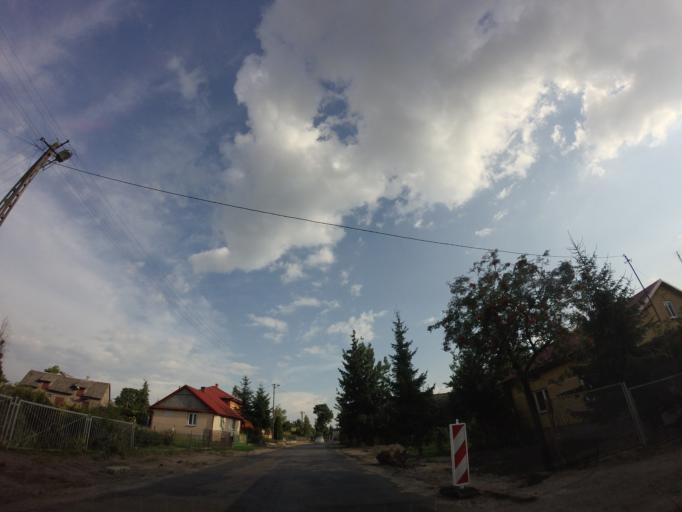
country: PL
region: Lublin Voivodeship
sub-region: Powiat lubartowski
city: Przytoczno
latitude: 51.6161
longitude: 22.2733
